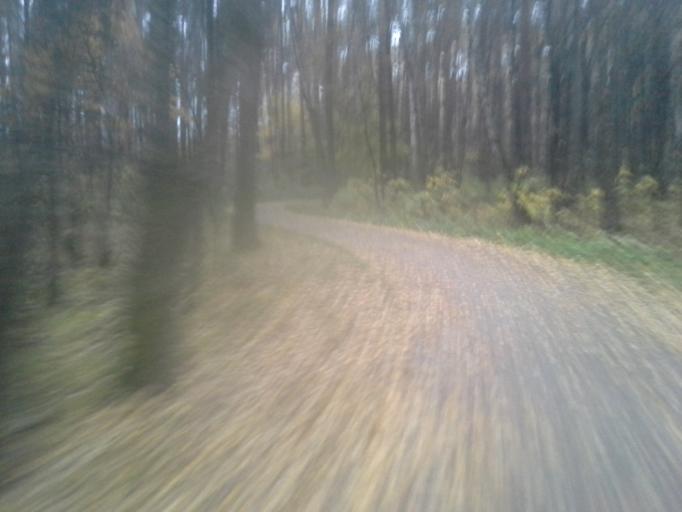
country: RU
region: Moskovskaya
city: Zarech'ye
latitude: 55.6659
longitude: 37.3832
